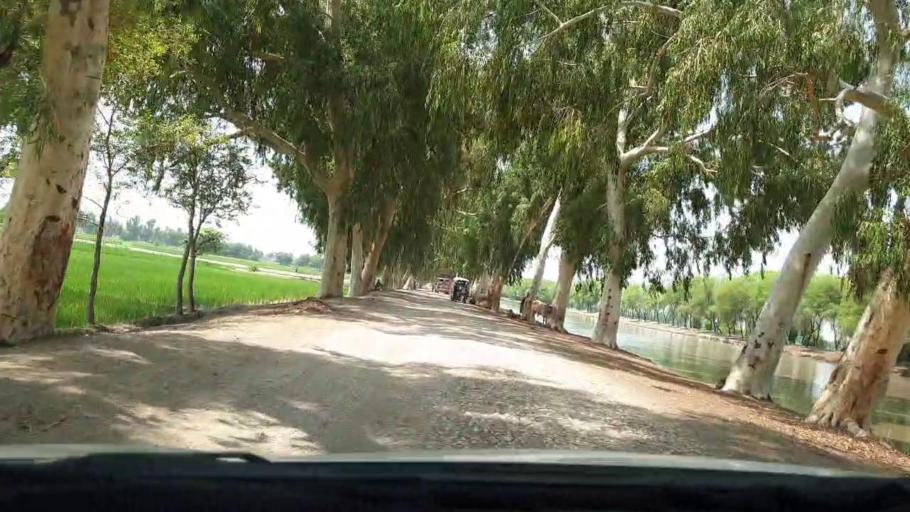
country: PK
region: Sindh
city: New Badah
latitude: 27.3019
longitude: 68.0916
